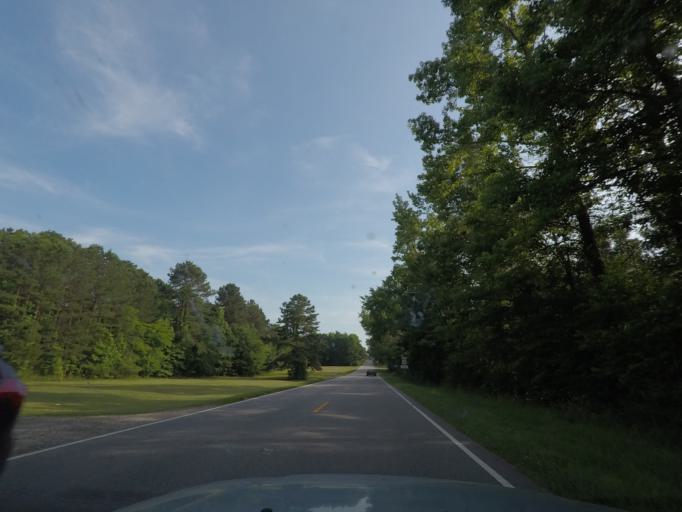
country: US
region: Virginia
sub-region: Mecklenburg County
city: Clarksville
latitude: 36.5046
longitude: -78.5387
